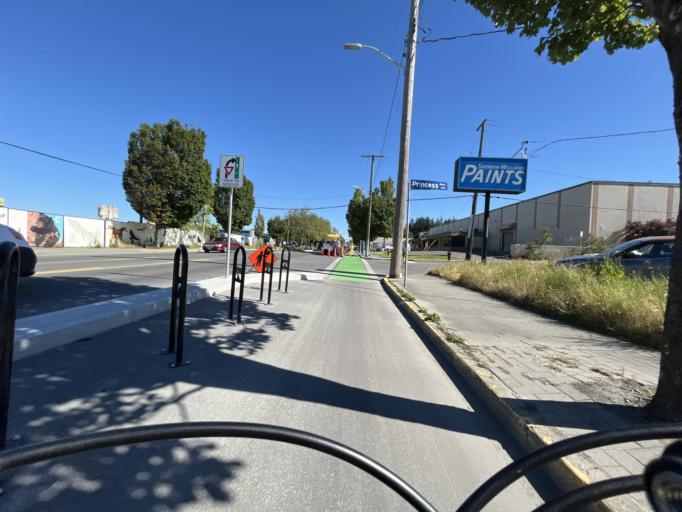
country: CA
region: British Columbia
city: Victoria
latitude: 48.4333
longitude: -123.3671
